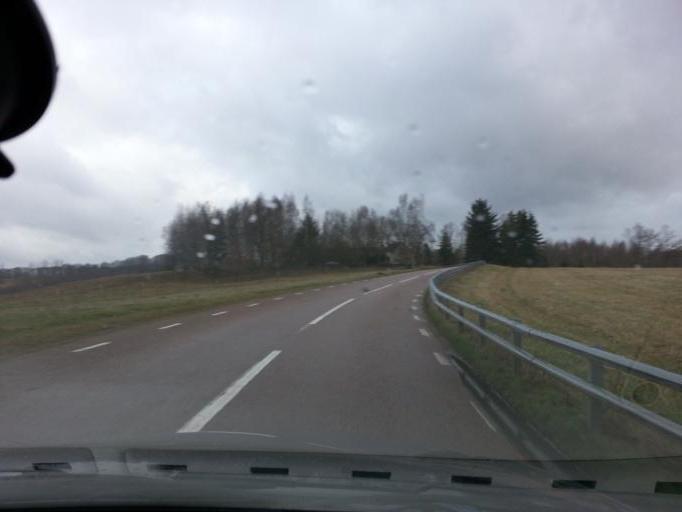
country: SE
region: Skane
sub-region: Klippans Kommun
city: Klippan
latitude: 56.1028
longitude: 13.1027
